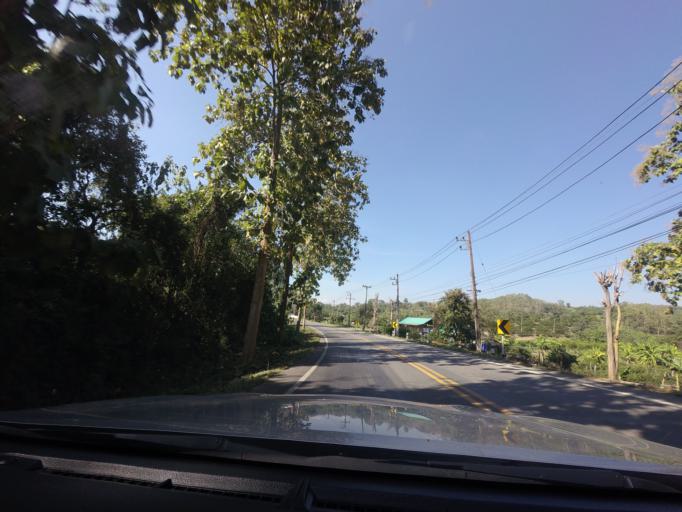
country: TH
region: Sukhothai
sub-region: Amphoe Si Satchanalai
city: Si Satchanalai
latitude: 17.6169
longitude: 99.7089
